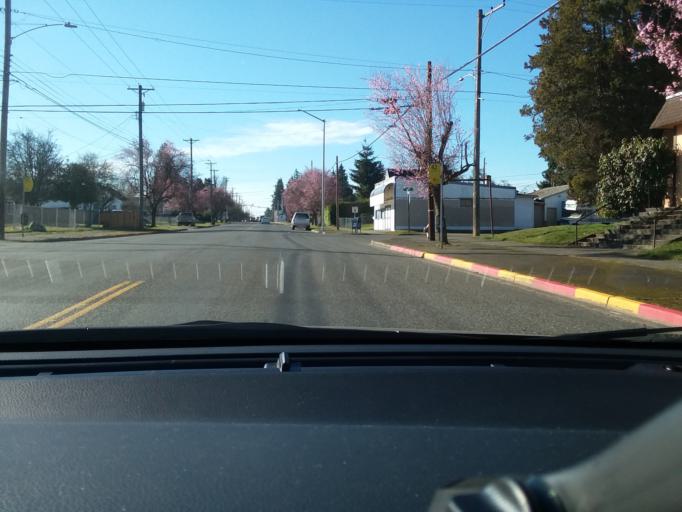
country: US
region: Washington
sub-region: Pierce County
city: Tacoma
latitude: 47.2156
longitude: -122.4210
